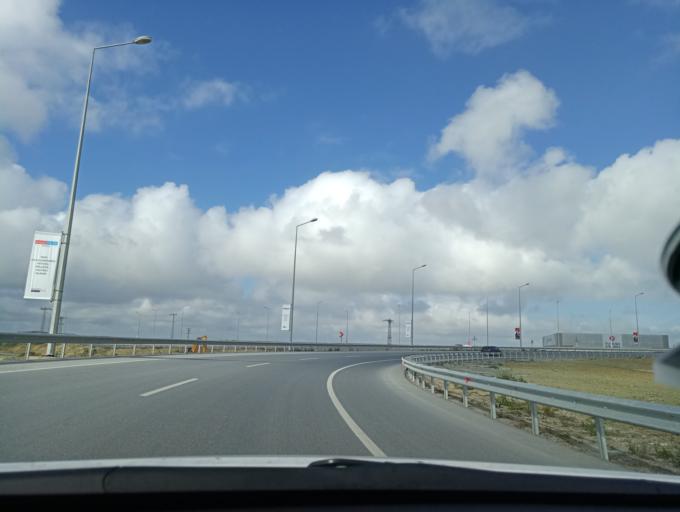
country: TR
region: Istanbul
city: Durusu
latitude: 41.2445
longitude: 28.7323
